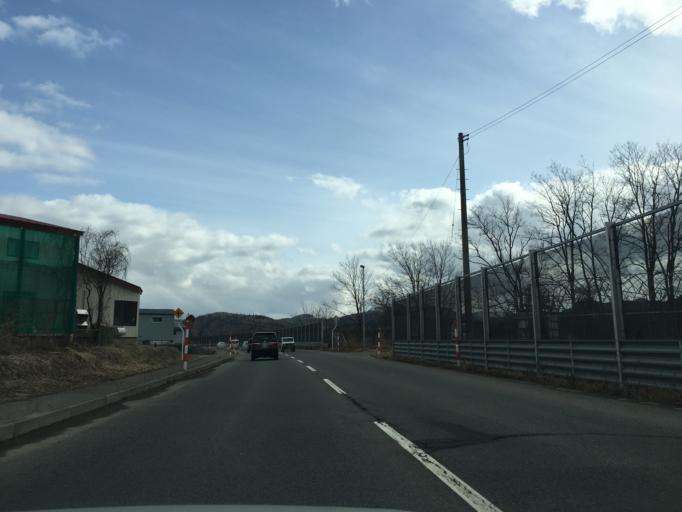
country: JP
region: Akita
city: Hanawa
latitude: 40.2325
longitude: 140.7017
